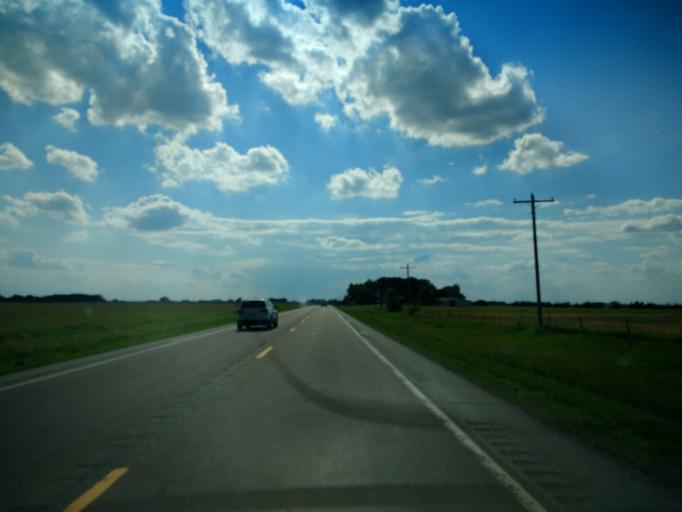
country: US
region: Iowa
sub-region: Clay County
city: Spencer
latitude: 43.1838
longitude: -95.2121
